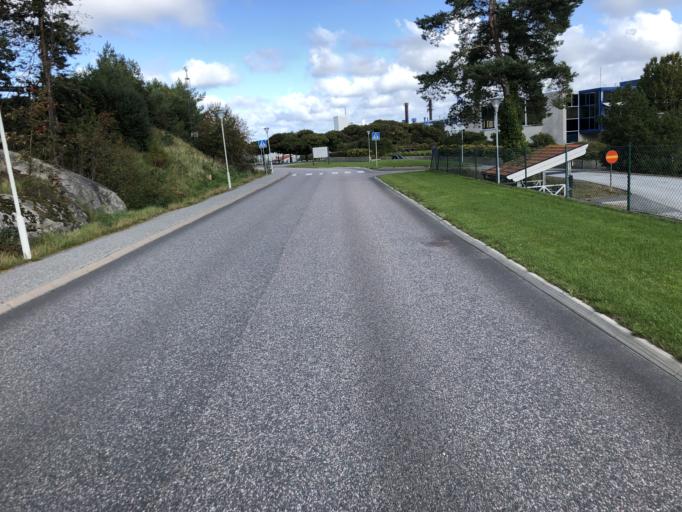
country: SE
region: Vaestra Goetaland
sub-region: Goteborg
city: Majorna
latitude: 57.7283
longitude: 11.8541
